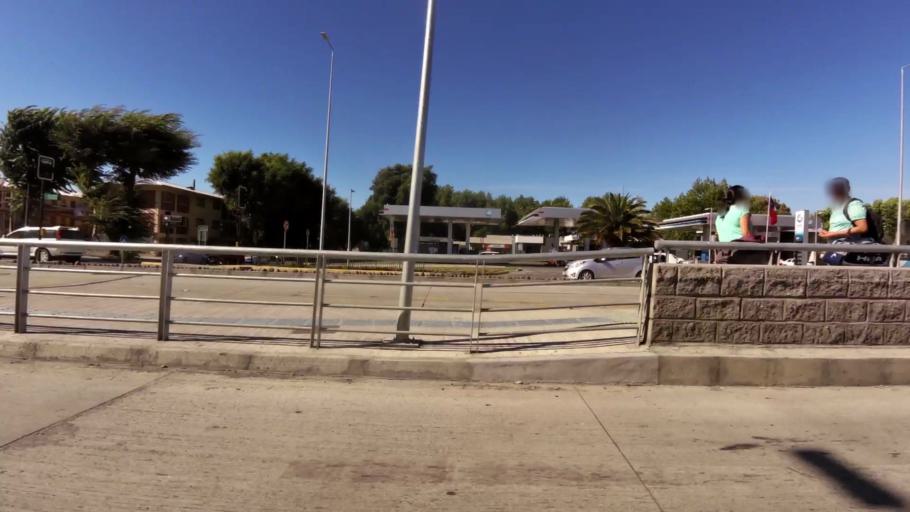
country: CL
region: Biobio
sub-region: Provincia de Concepcion
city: Concepcion
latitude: -36.8107
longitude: -73.0739
